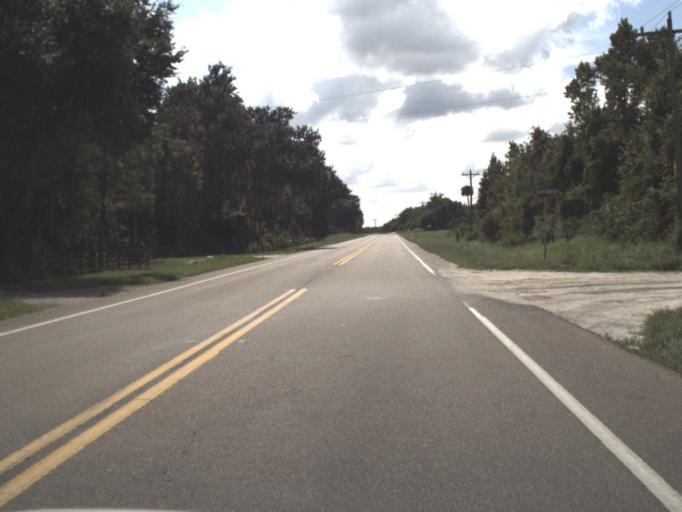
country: US
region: Florida
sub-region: Hardee County
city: Zolfo Springs
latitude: 27.4895
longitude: -81.8415
